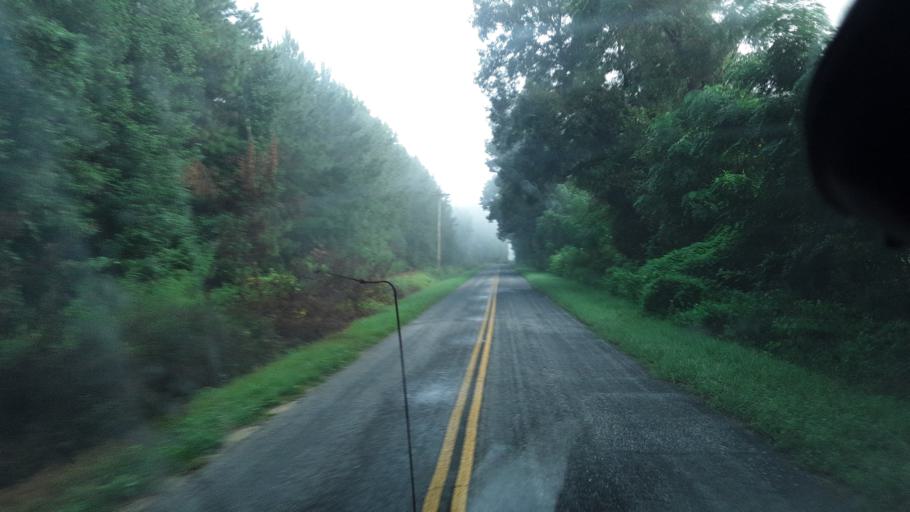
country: US
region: South Carolina
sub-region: Williamsburg County
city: Kingstree
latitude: 33.8149
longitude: -79.9628
